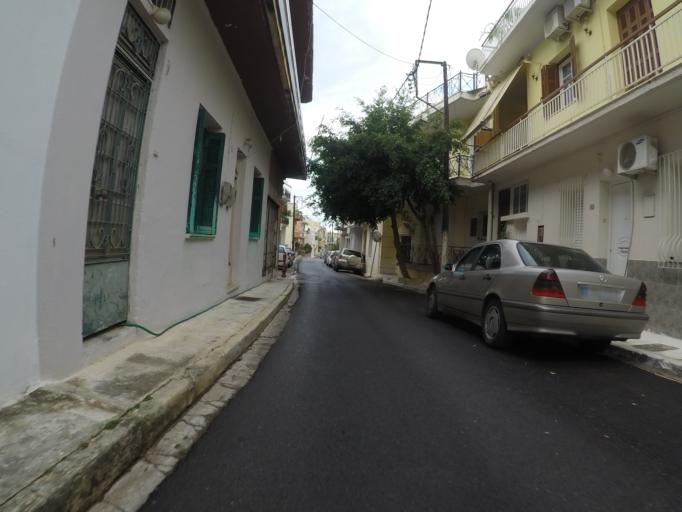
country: GR
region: Peloponnese
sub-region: Nomos Messinias
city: Kalamata
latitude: 37.0428
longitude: 22.1051
